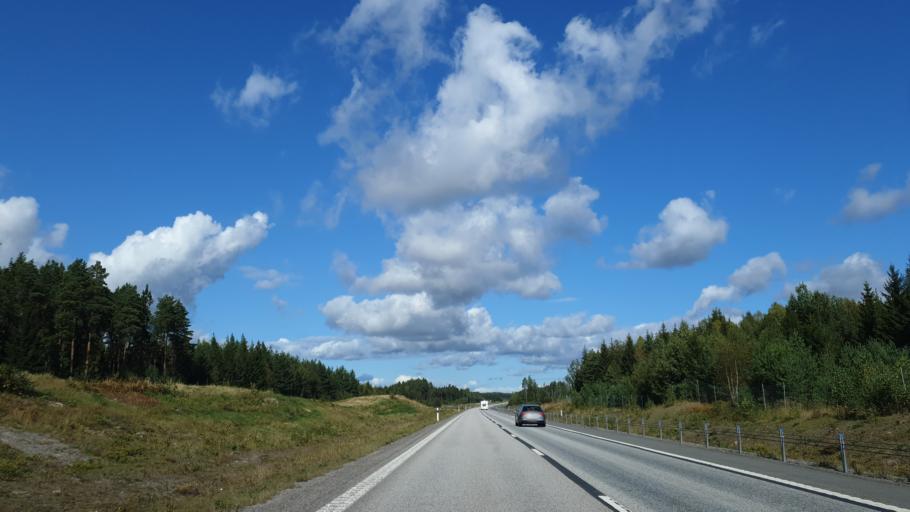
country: SE
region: Uppsala
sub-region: Tierps Kommun
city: Tierp
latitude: 60.2577
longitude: 17.5005
